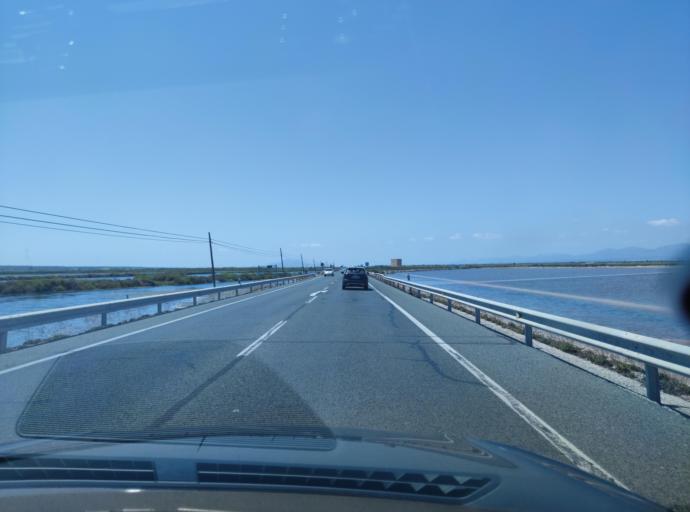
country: ES
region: Valencia
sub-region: Provincia de Alicante
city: Santa Pola
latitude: 38.1852
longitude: -0.6086
